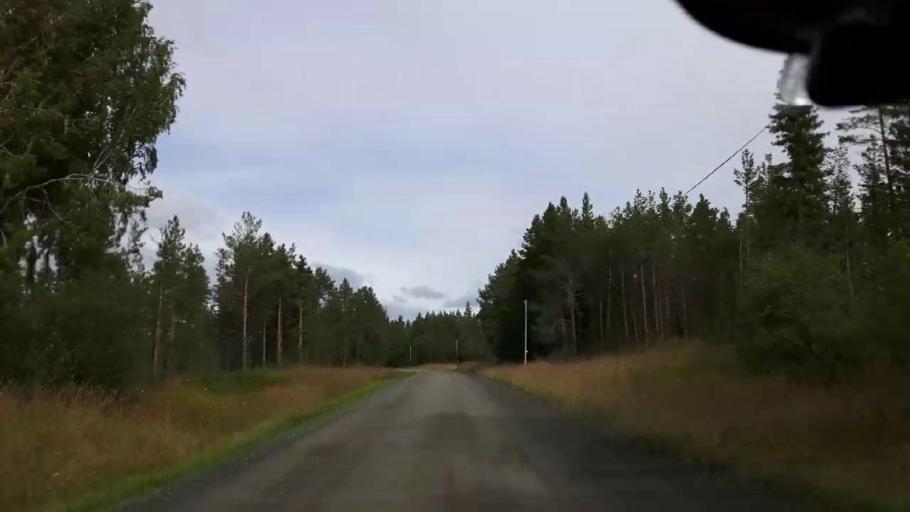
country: SE
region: Jaemtland
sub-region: Krokoms Kommun
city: Krokom
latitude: 63.3725
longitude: 14.1293
